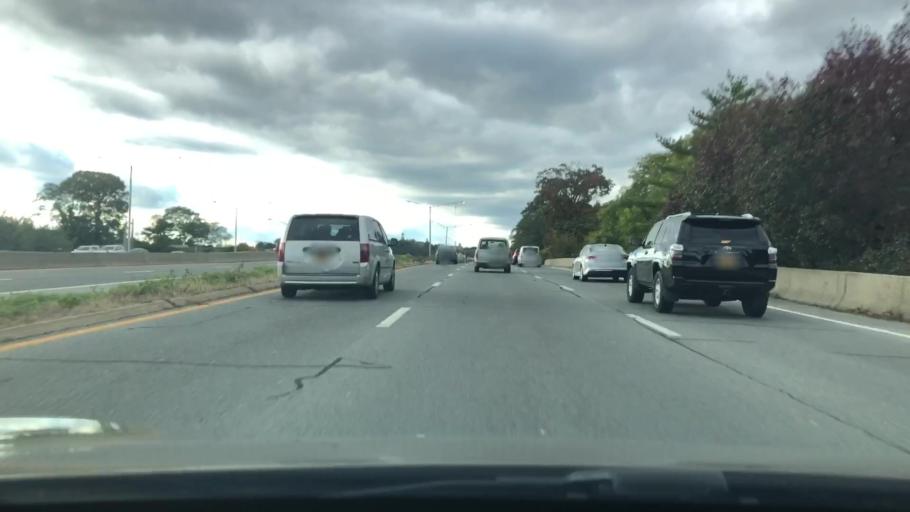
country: US
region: New York
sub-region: Westchester County
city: Bronxville
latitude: 40.9297
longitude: -73.8472
